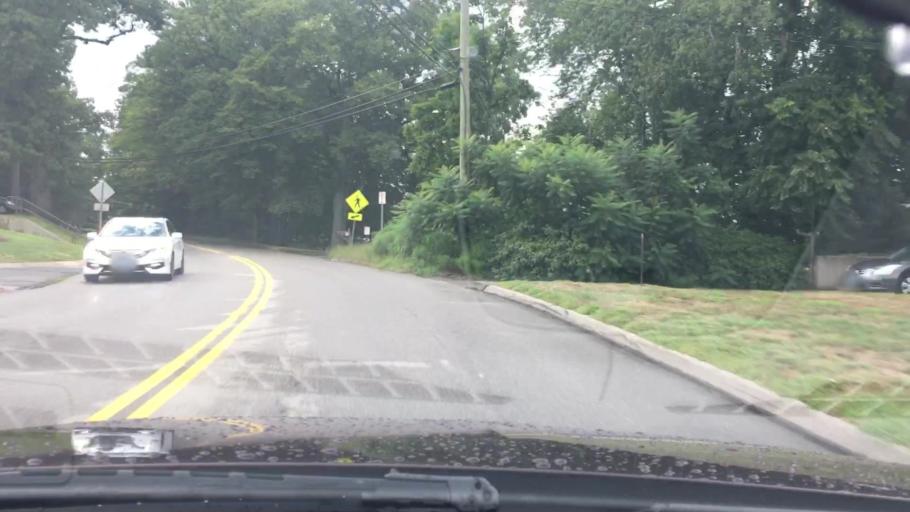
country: US
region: Connecticut
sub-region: Hartford County
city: Glastonbury Center
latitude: 41.7131
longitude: -72.5856
